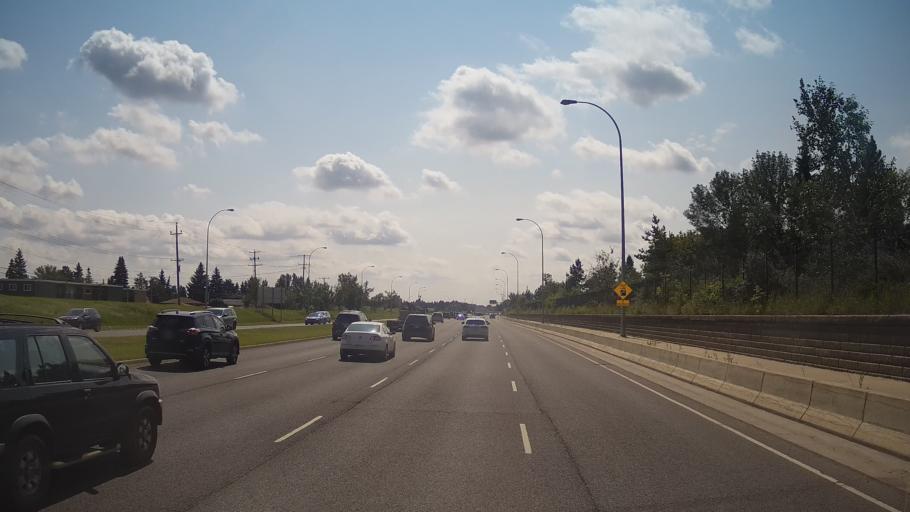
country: CA
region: Alberta
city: St. Albert
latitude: 53.5183
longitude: -113.6156
